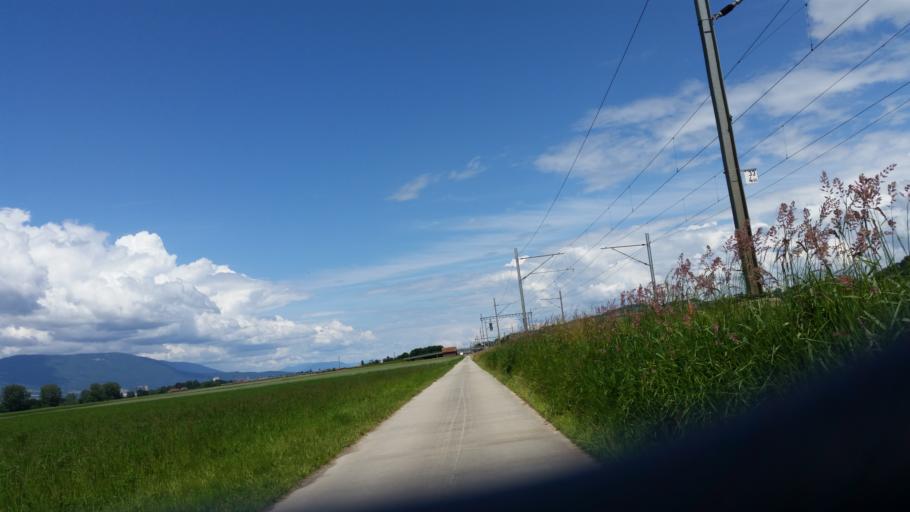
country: CH
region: Vaud
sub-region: Jura-Nord vaudois District
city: Yverdon-les-Bains
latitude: 46.7511
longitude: 6.6153
